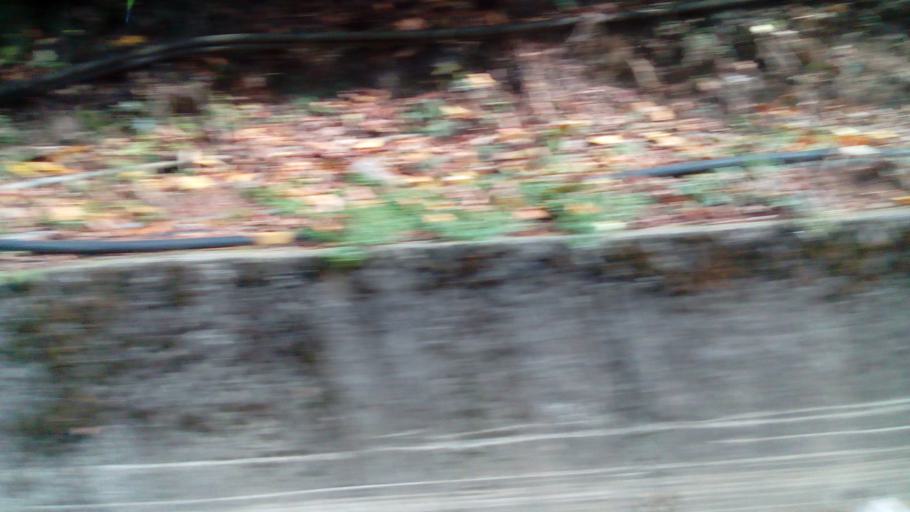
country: TW
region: Taiwan
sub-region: Hualien
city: Hualian
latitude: 24.3286
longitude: 121.3080
